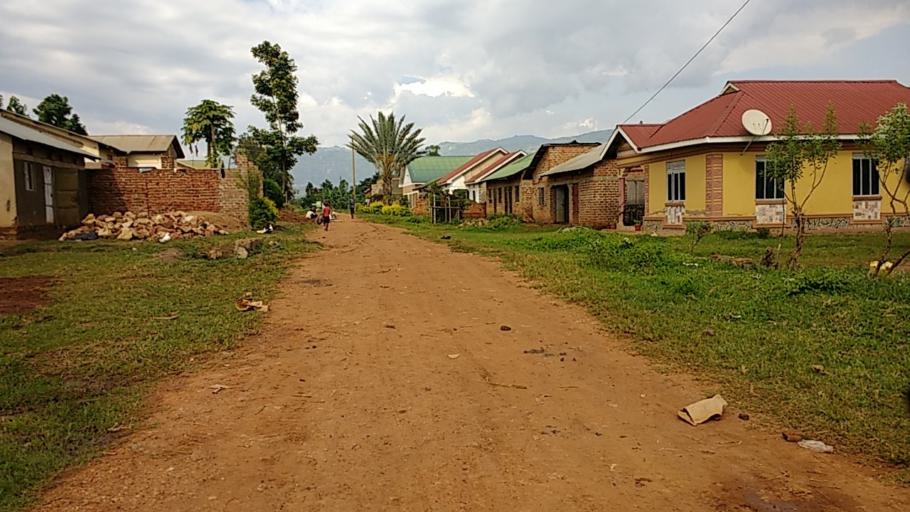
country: UG
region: Eastern Region
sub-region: Mbale District
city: Mbale
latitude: 1.0660
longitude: 34.1630
